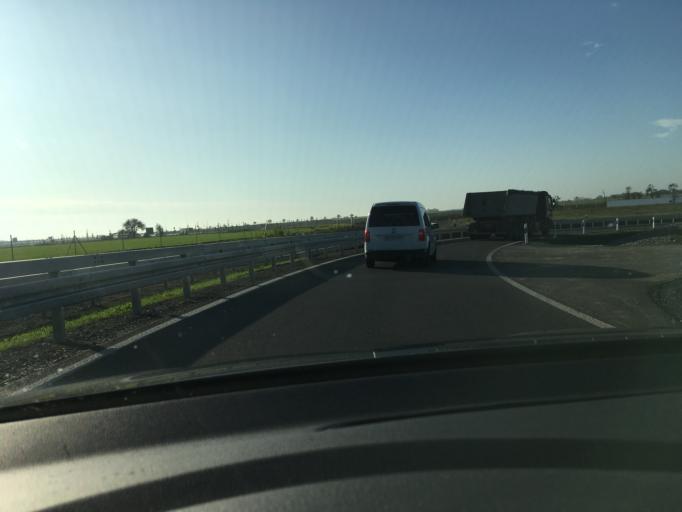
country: DE
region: Saxony
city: Espenhain
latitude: 51.1950
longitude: 12.4452
